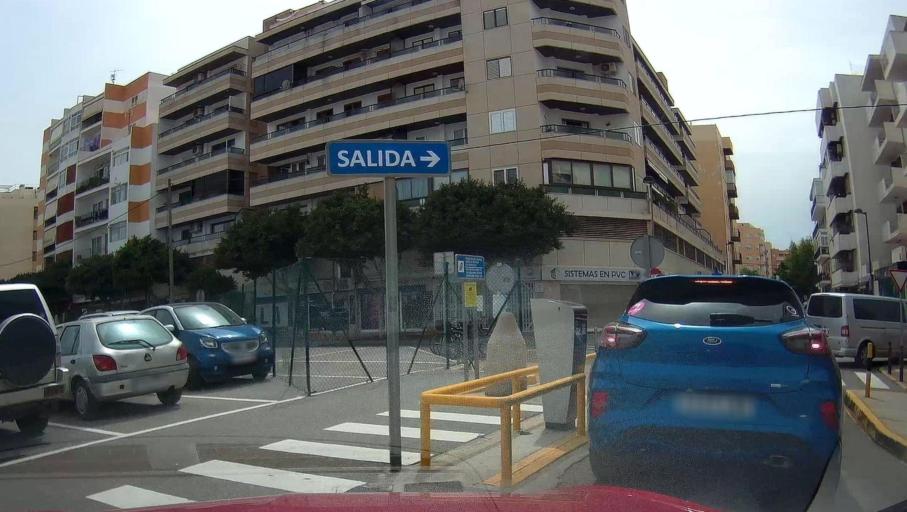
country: ES
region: Balearic Islands
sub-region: Illes Balears
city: Ibiza
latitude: 38.9141
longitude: 1.4308
